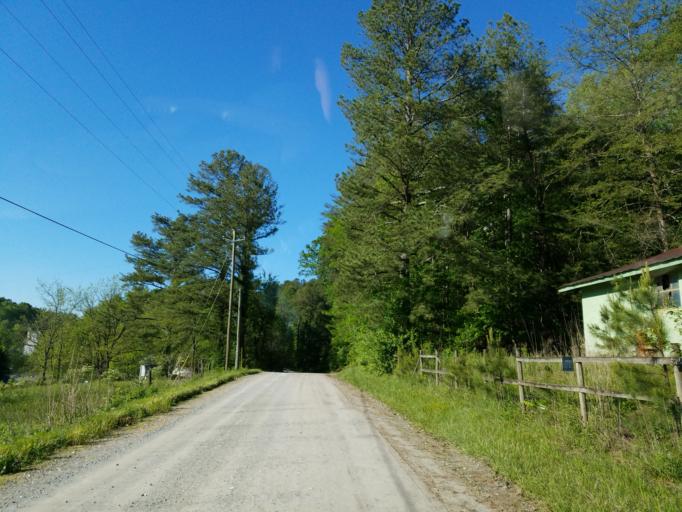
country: US
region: Georgia
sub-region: Gilmer County
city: Ellijay
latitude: 34.6094
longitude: -84.5045
